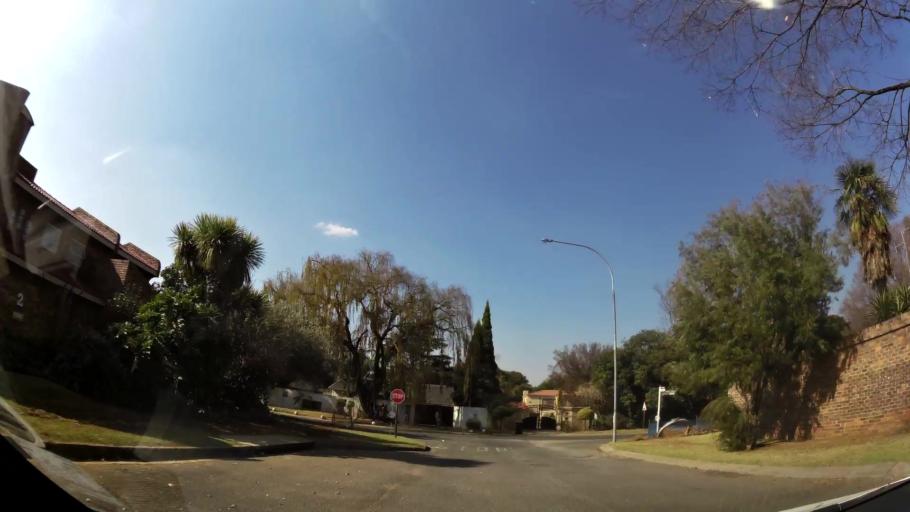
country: ZA
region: Gauteng
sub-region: Ekurhuleni Metropolitan Municipality
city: Benoni
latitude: -26.1821
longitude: 28.2840
